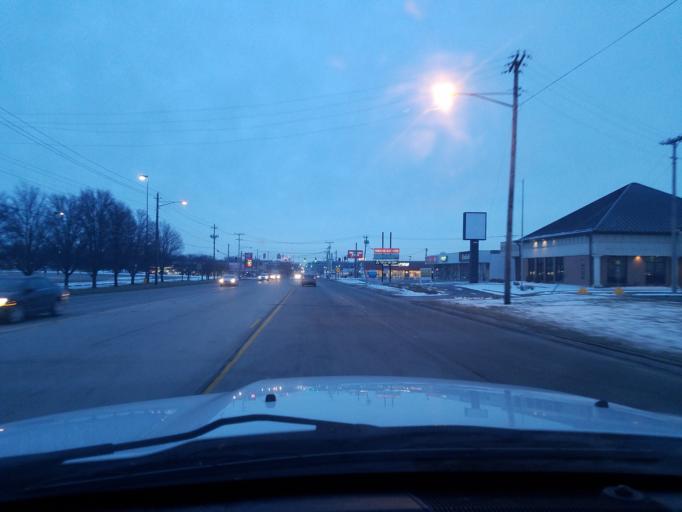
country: US
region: Indiana
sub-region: Delaware County
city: Muncie
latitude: 40.2190
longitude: -85.3763
